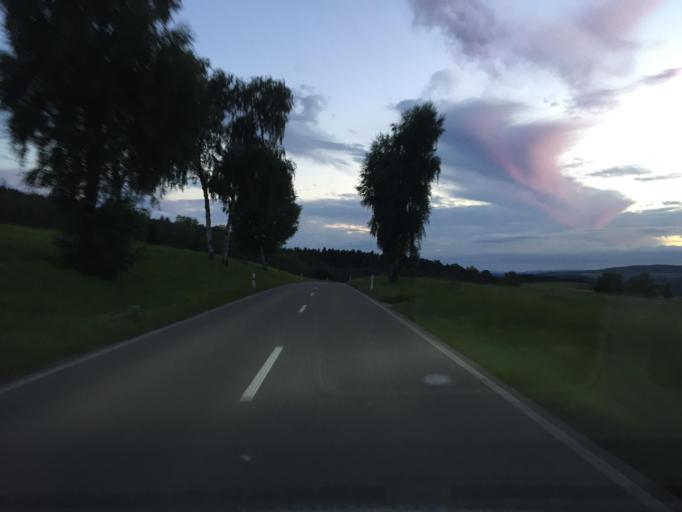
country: DE
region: Baden-Wuerttemberg
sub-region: Freiburg Region
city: Wutoschingen
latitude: 47.6649
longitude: 8.4013
